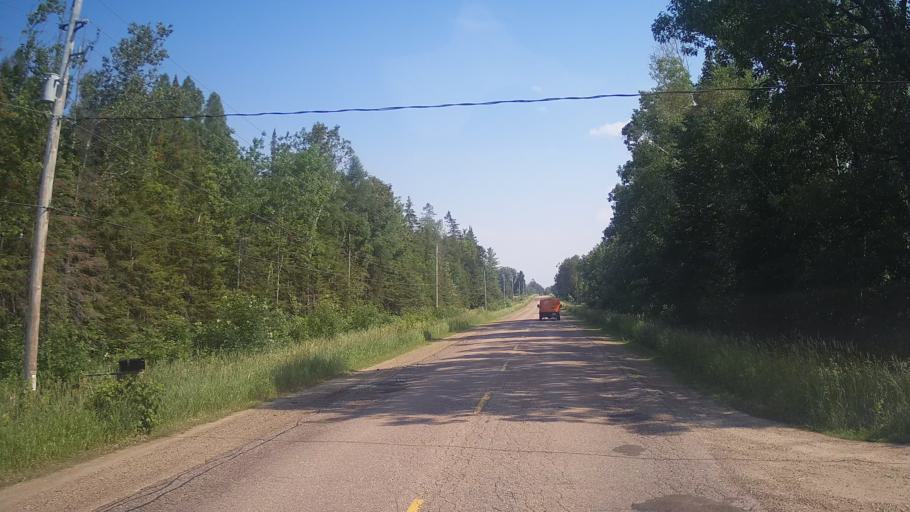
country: CA
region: Ontario
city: Pembroke
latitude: 45.5971
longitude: -77.2313
